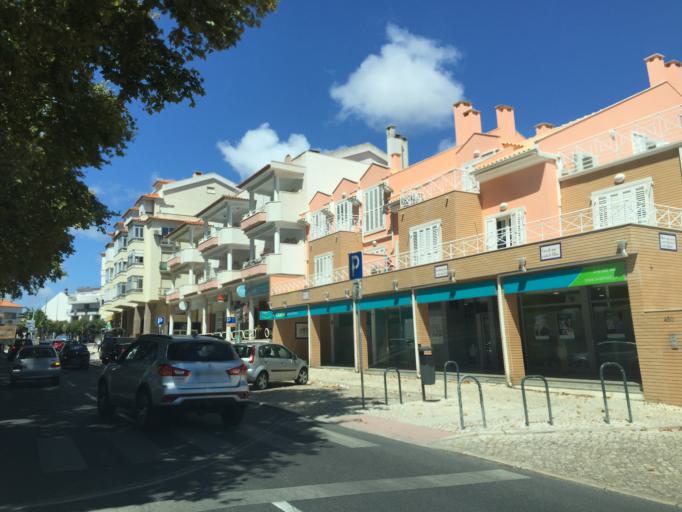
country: PT
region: Lisbon
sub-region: Cascais
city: Parede
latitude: 38.6900
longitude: -9.3511
